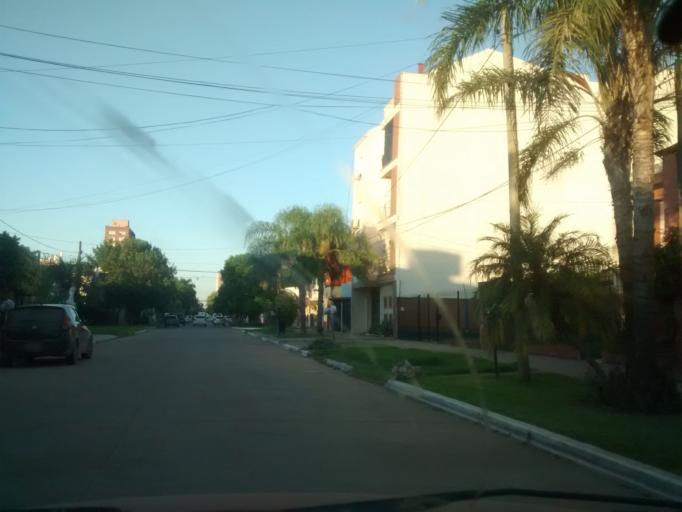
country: AR
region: Chaco
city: Resistencia
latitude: -27.4586
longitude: -58.9983
